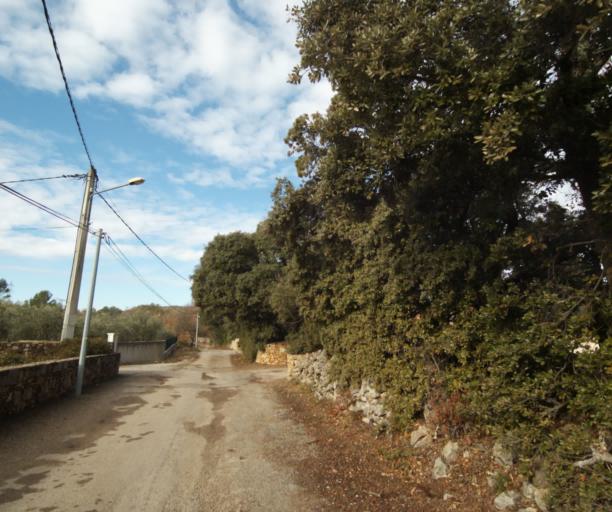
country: FR
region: Provence-Alpes-Cote d'Azur
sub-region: Departement du Var
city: Trans-en-Provence
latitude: 43.5055
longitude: 6.4771
